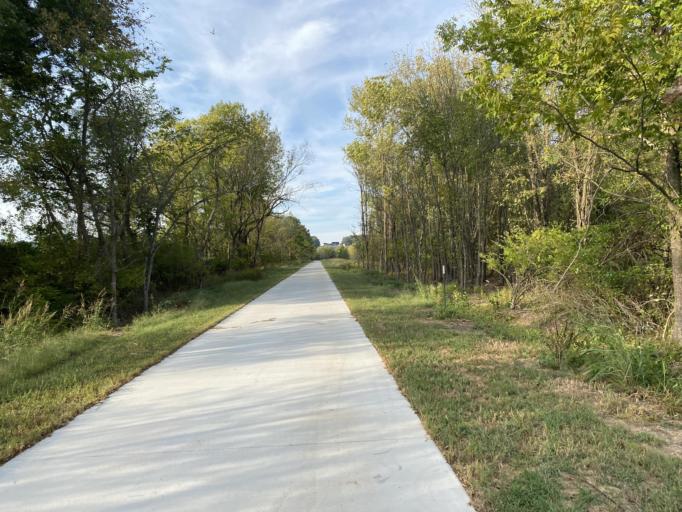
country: US
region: Arkansas
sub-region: Washington County
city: Johnson
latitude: 36.1066
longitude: -94.1942
